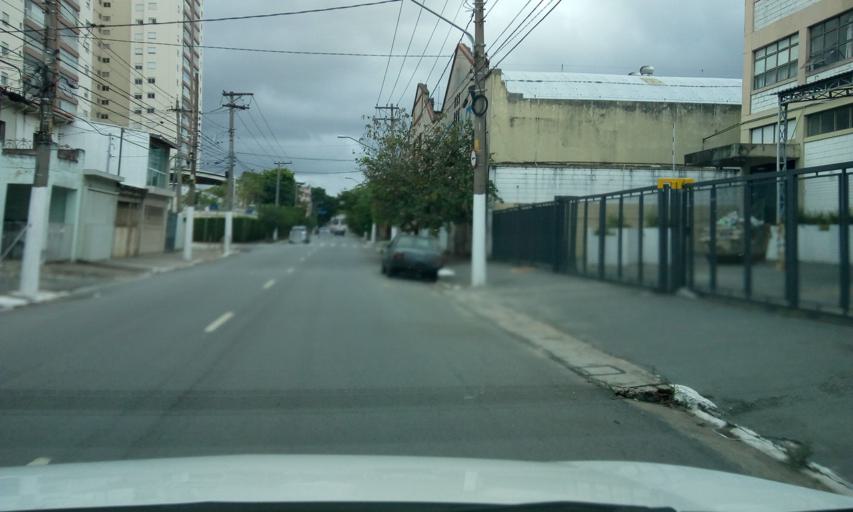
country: BR
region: Sao Paulo
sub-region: Sao Paulo
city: Sao Paulo
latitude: -23.5624
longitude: -46.6050
